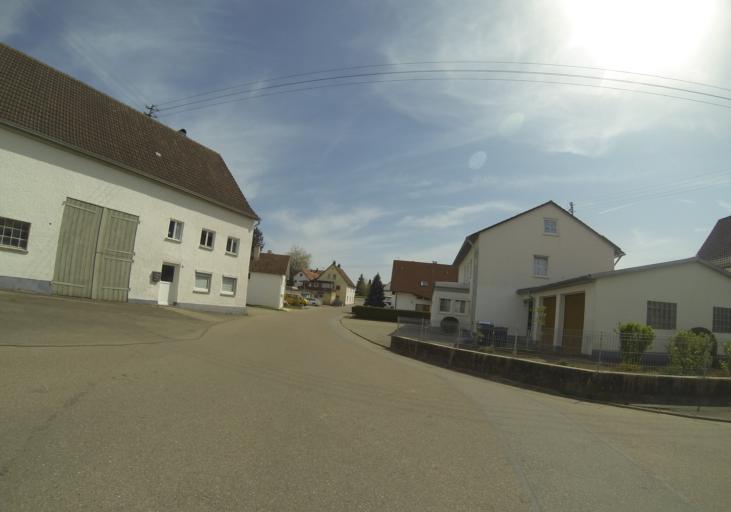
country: DE
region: Baden-Wuerttemberg
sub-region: Tuebingen Region
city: Huttisheim
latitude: 48.2602
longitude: 9.9268
